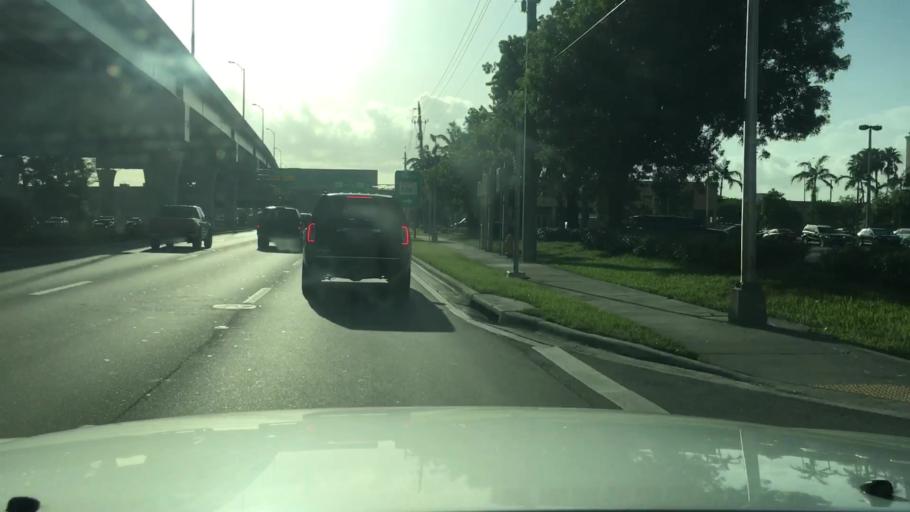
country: US
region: Florida
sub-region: Miami-Dade County
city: Virginia Gardens
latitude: 25.7966
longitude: -80.3237
